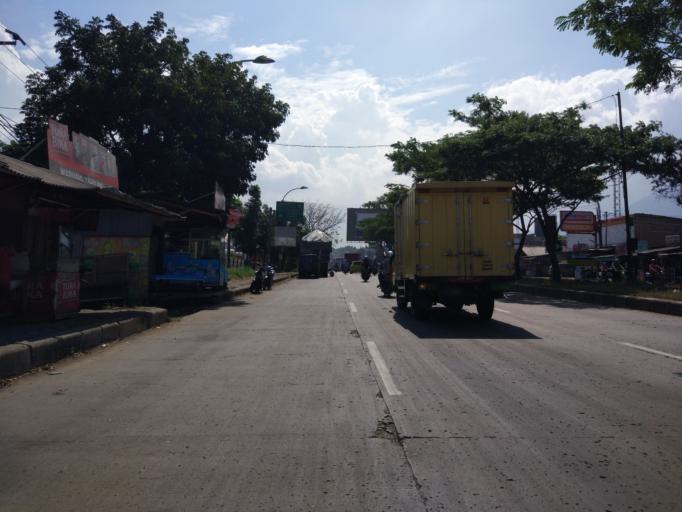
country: ID
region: West Java
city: Cileunyi
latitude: -6.9433
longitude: 107.7564
